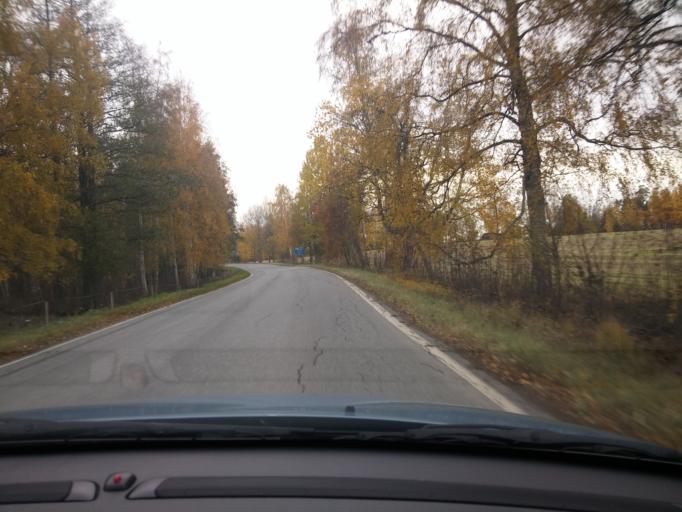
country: FI
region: Haeme
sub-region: Forssa
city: Tammela
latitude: 60.7971
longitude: 23.8141
